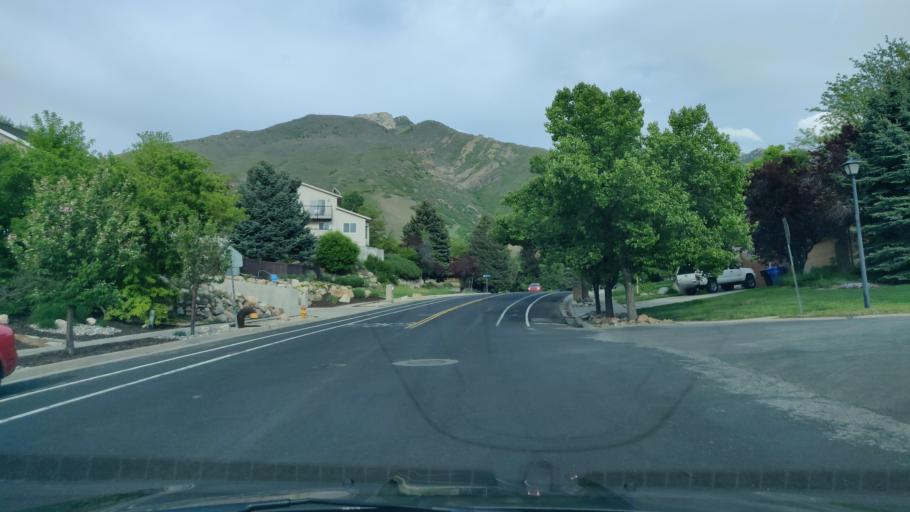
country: US
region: Utah
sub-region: Salt Lake County
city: Cottonwood Heights
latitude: 40.6049
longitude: -111.8017
